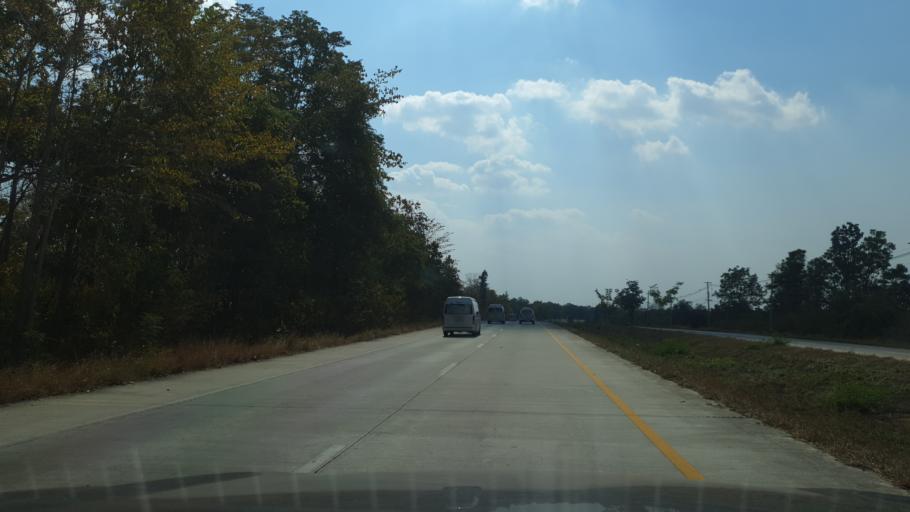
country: TH
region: Tak
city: Sam Ngao
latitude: 17.3081
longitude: 99.1485
